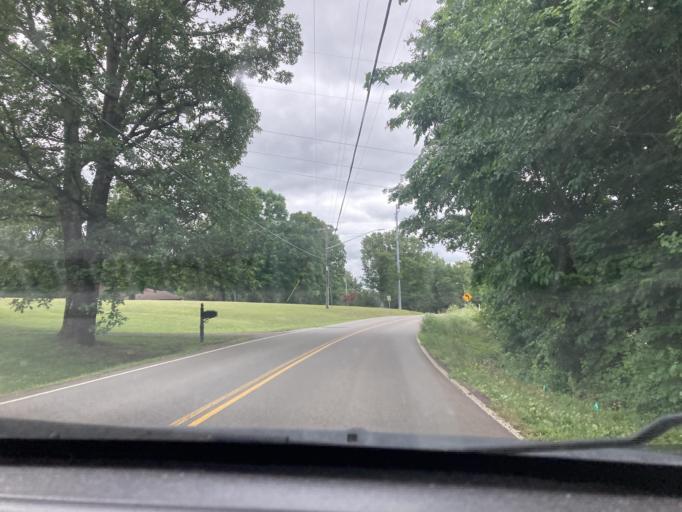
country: US
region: Tennessee
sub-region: Dickson County
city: Dickson
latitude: 36.0973
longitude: -87.3805
